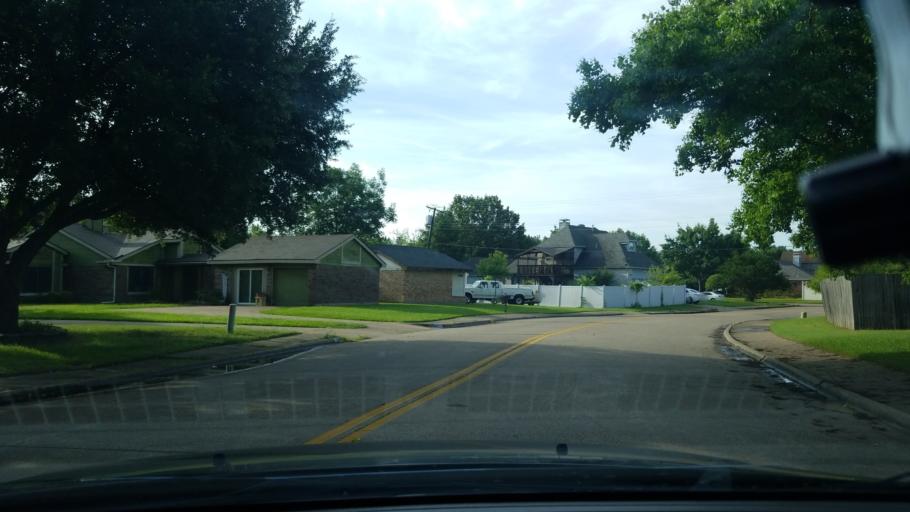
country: US
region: Texas
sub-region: Dallas County
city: Mesquite
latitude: 32.8018
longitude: -96.6008
